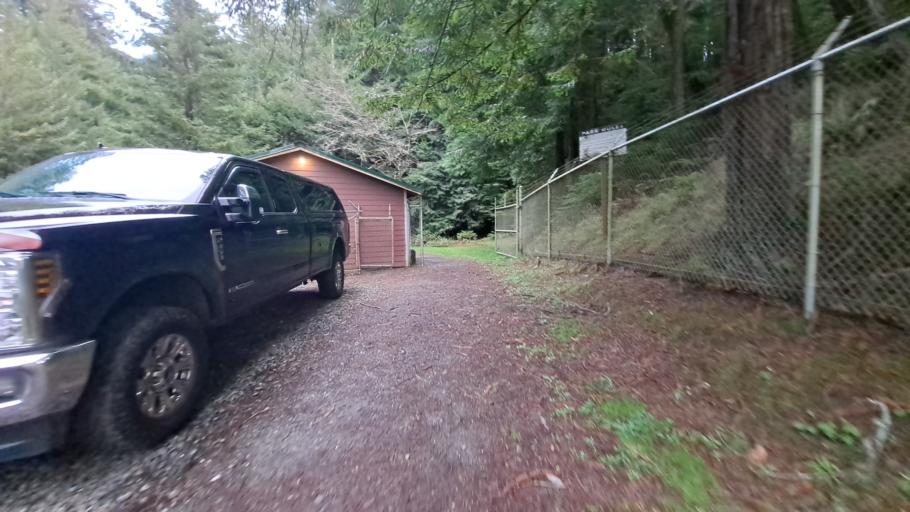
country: US
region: California
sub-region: Humboldt County
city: Fortuna
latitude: 40.6022
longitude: -124.1483
